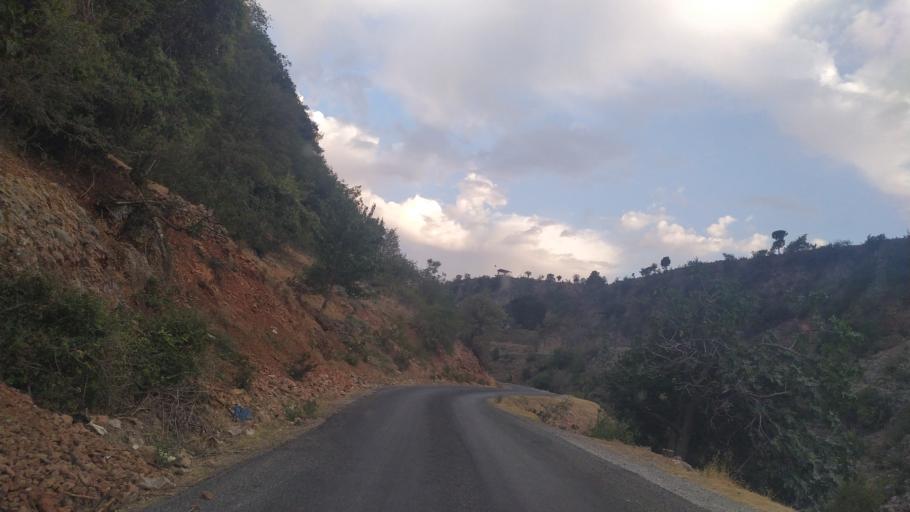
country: TR
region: Mersin
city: Camliyayla
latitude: 37.2398
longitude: 34.7140
